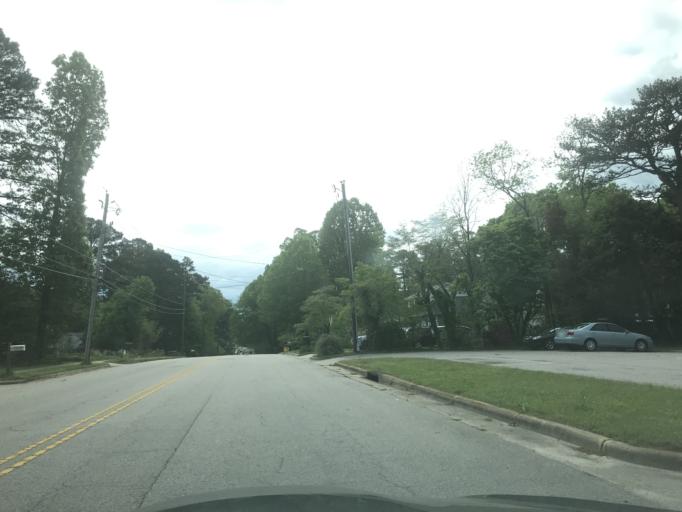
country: US
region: North Carolina
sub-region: Wake County
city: West Raleigh
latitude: 35.7840
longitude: -78.7128
